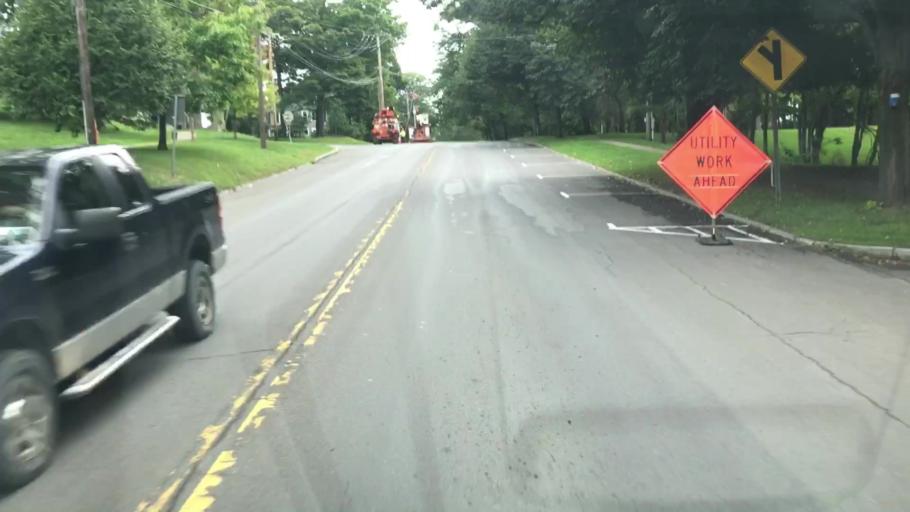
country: US
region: New York
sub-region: Onondaga County
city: Skaneateles
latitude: 42.9451
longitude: -76.4236
